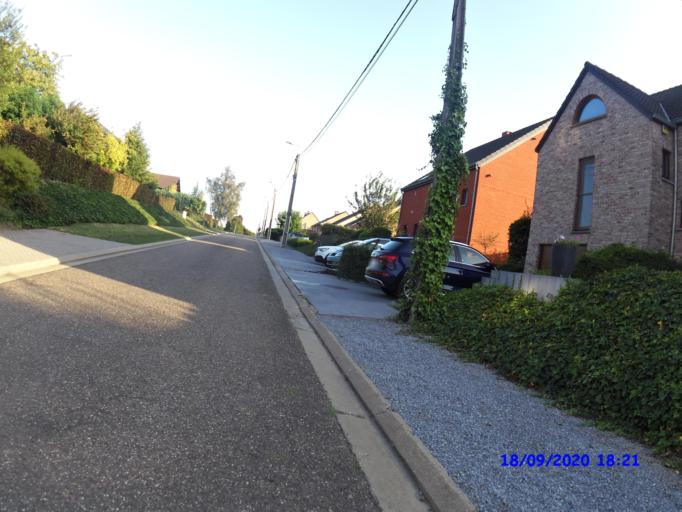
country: BE
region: Wallonia
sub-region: Province de Liege
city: Berloz
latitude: 50.6999
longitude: 5.2209
